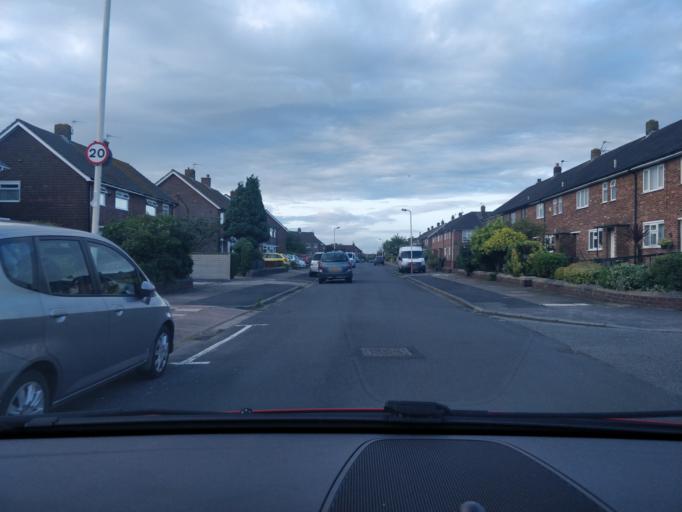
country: GB
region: England
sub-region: Sefton
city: Southport
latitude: 53.6631
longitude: -2.9779
